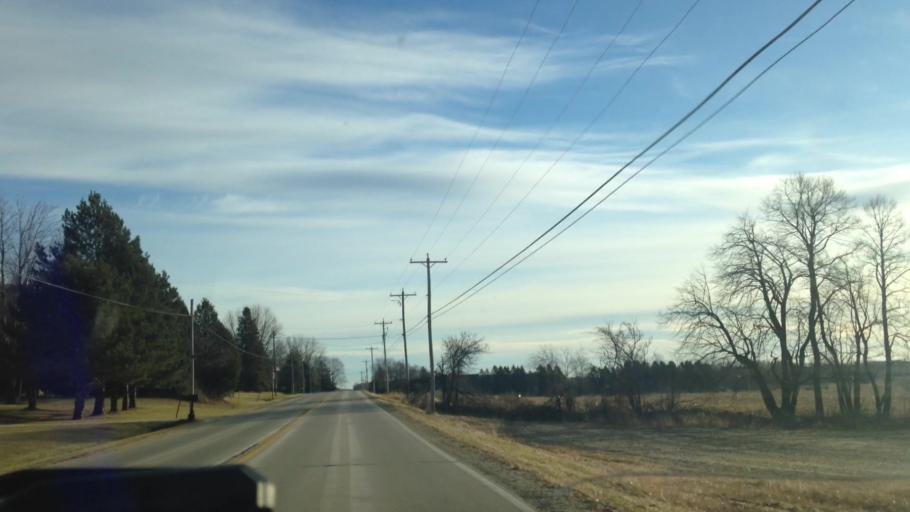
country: US
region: Wisconsin
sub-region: Washington County
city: Jackson
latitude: 43.2945
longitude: -88.1285
